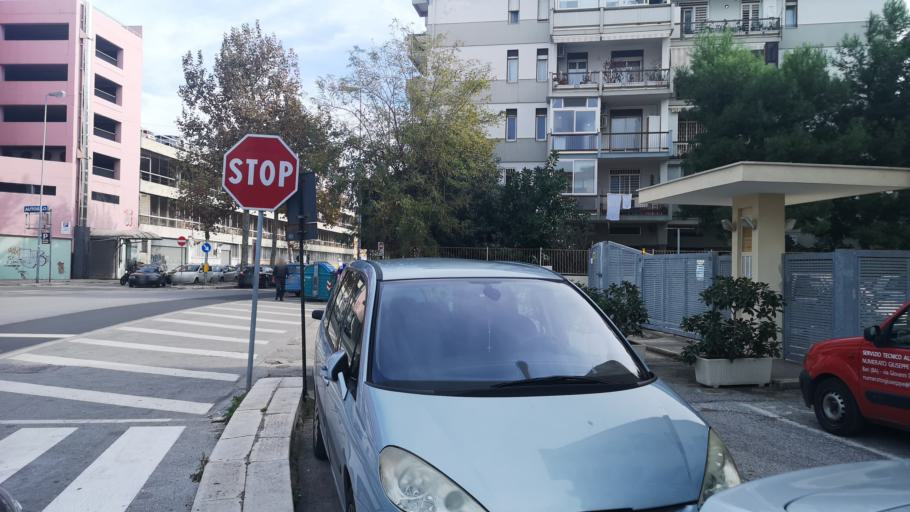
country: IT
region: Apulia
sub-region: Provincia di Bari
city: Bari
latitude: 41.1157
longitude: 16.8853
